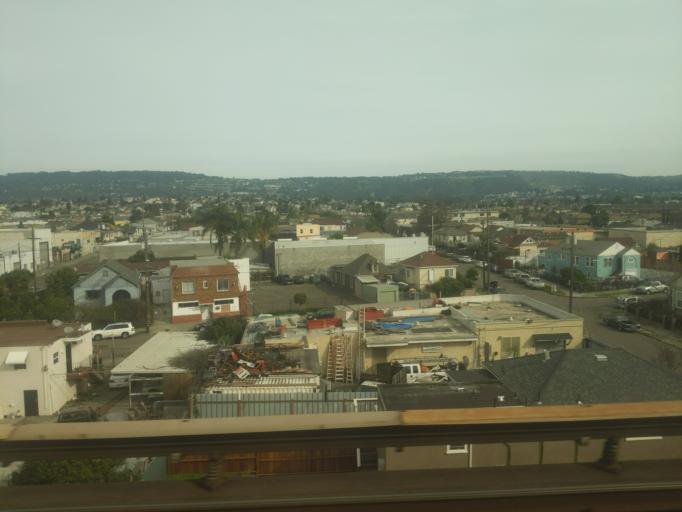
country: US
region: California
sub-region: Alameda County
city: Alameda
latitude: 37.7657
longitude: -122.2110
